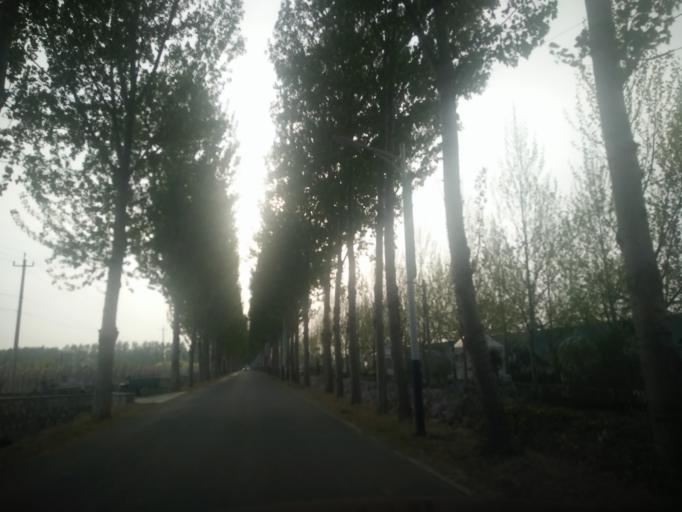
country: CN
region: Beijing
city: Weishanzhuang
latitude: 39.6758
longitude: 116.4430
